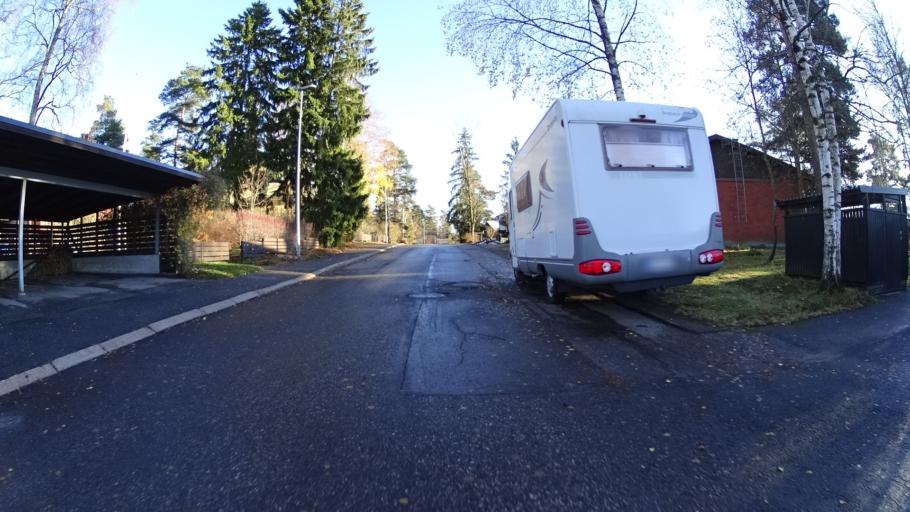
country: FI
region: Uusimaa
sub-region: Helsinki
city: Teekkarikylae
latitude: 60.2322
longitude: 24.8395
